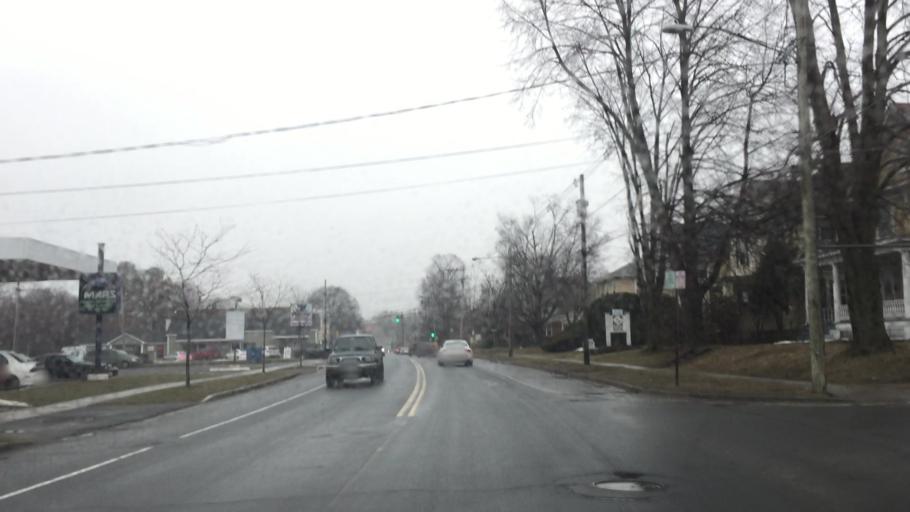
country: US
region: Massachusetts
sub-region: Berkshire County
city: Pittsfield
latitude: 42.4445
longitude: -73.2428
